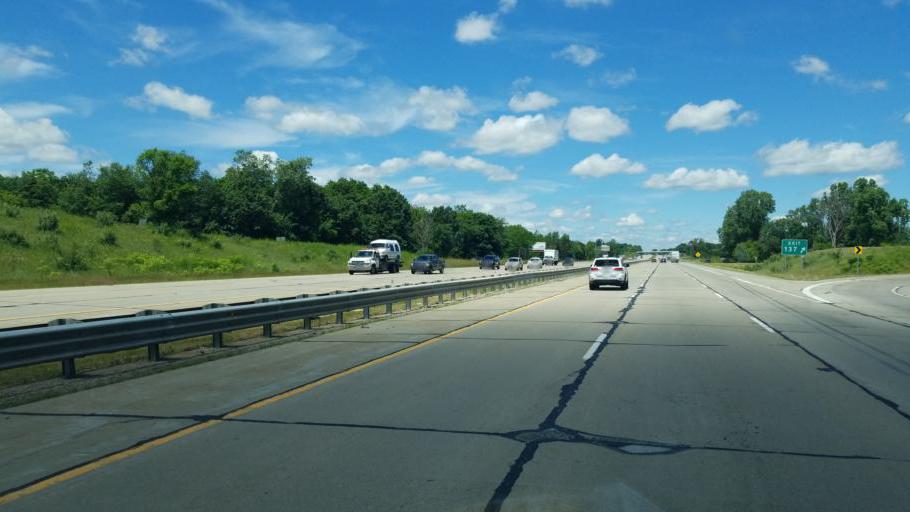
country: US
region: Michigan
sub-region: Livingston County
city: Howell
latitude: 42.5910
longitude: -83.9345
